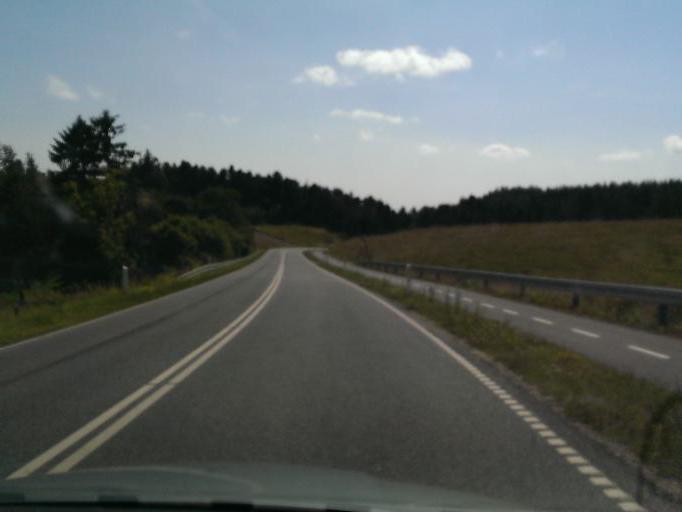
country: DK
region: Central Jutland
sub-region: Syddjurs Kommune
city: Ronde
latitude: 56.2460
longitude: 10.5634
